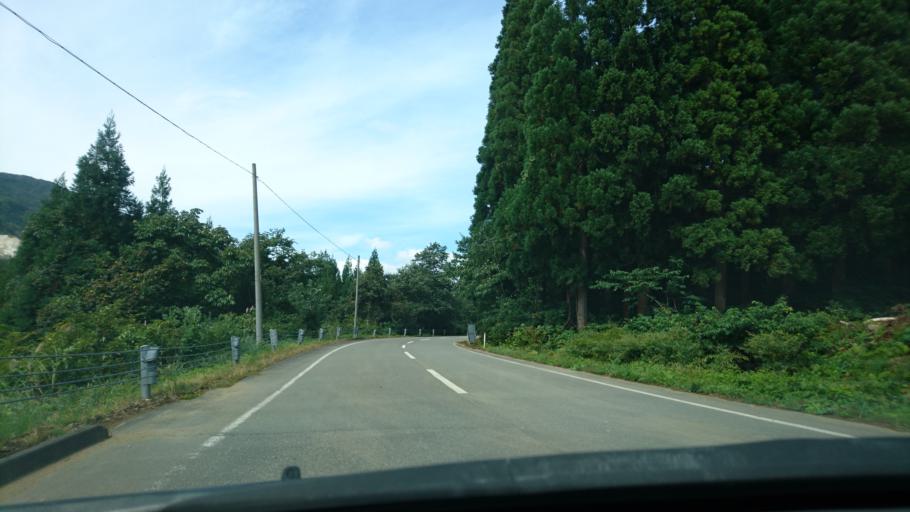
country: JP
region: Akita
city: Yuzawa
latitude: 39.0283
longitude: 140.7280
